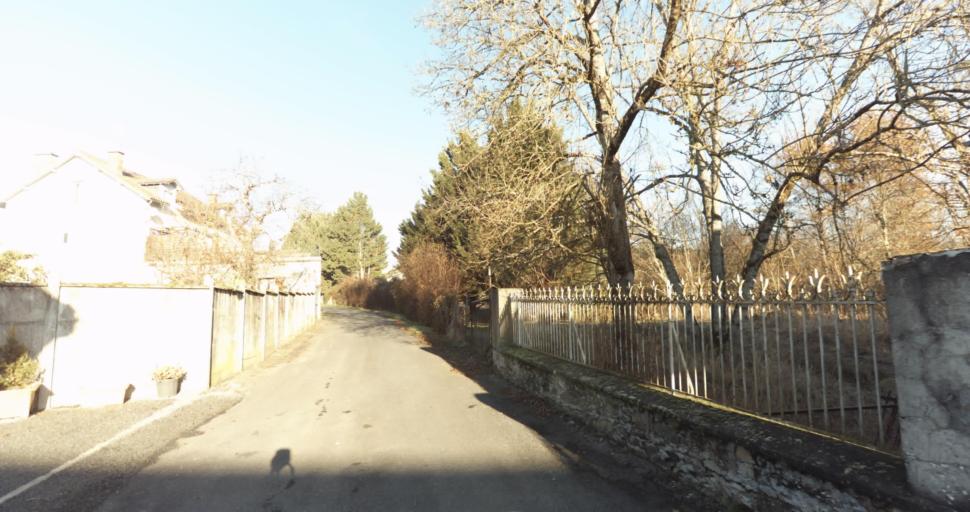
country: FR
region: Limousin
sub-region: Departement de la Haute-Vienne
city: Aixe-sur-Vienne
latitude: 45.7965
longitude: 1.1494
